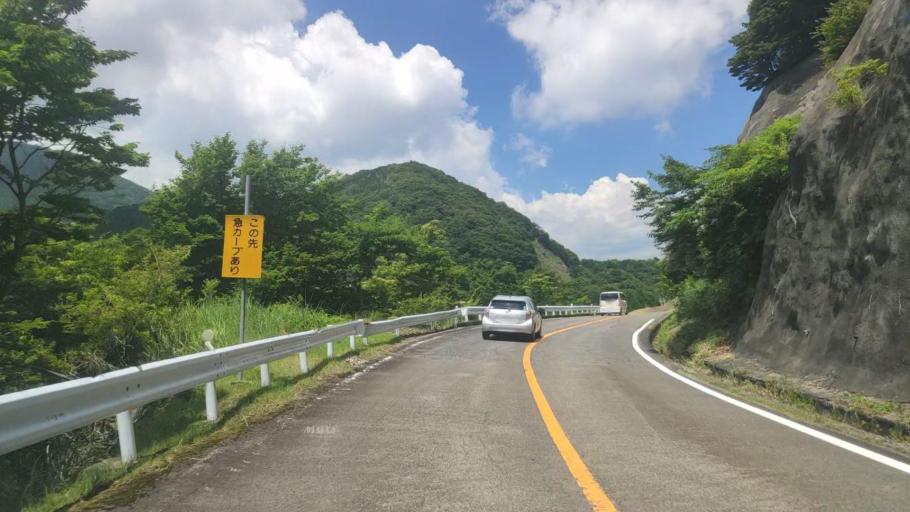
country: JP
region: Gifu
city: Tarui
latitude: 35.4031
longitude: 136.4248
